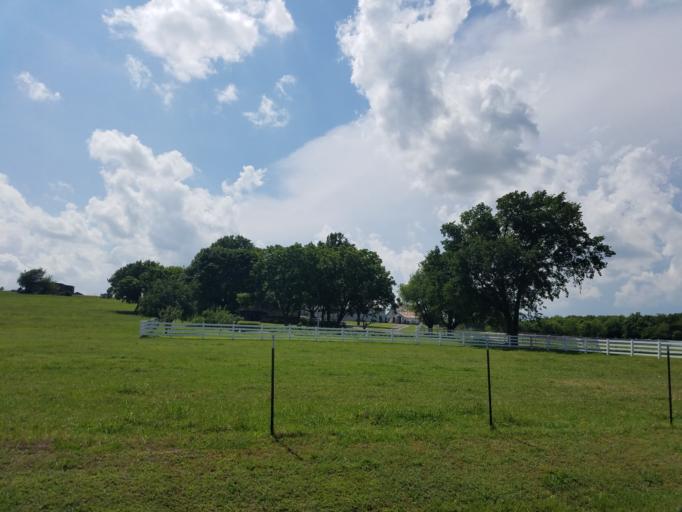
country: US
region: Oklahoma
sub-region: Mayes County
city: Chouteau
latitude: 36.1625
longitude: -95.3868
